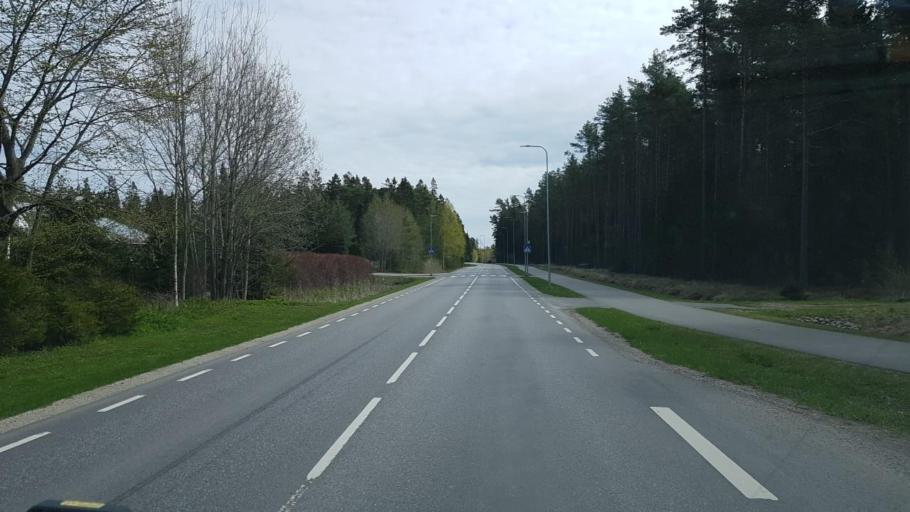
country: EE
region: Harju
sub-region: Viimsi vald
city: Haabneeme
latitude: 59.5459
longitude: 24.8410
